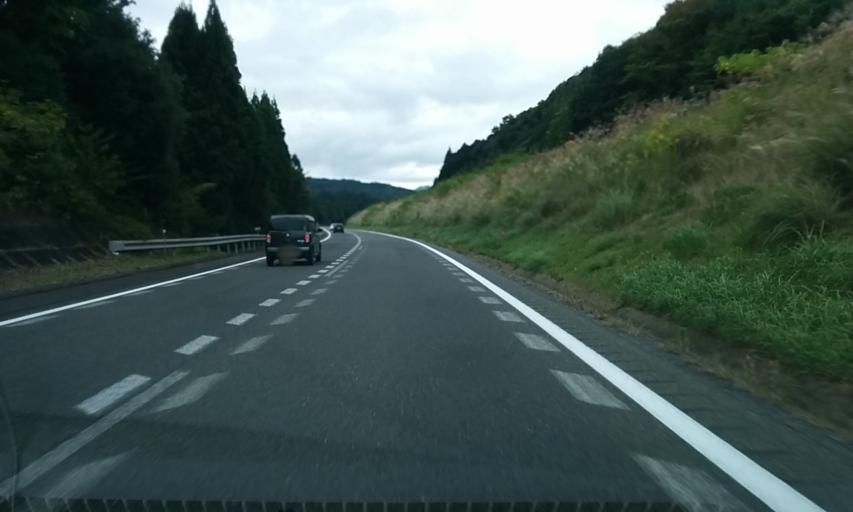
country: JP
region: Hyogo
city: Sasayama
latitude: 35.1091
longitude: 135.1673
